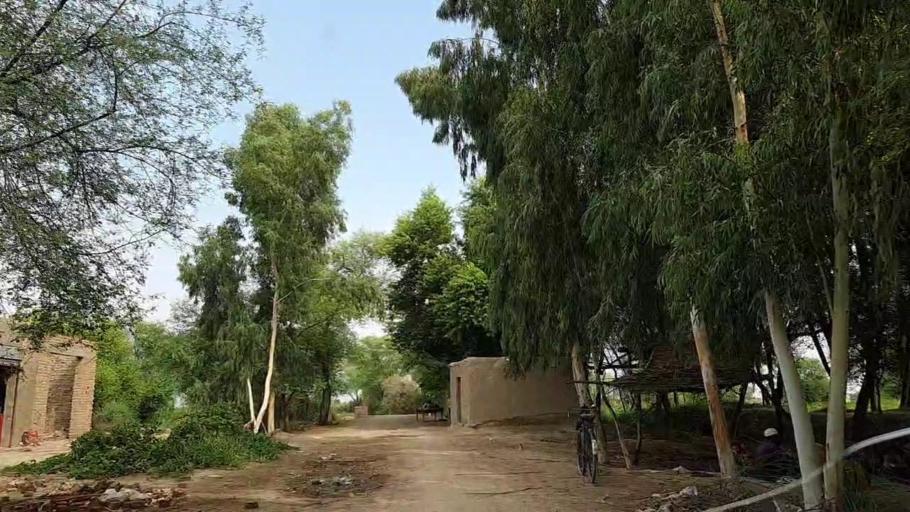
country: PK
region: Sindh
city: Khanpur
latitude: 27.8322
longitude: 69.5047
